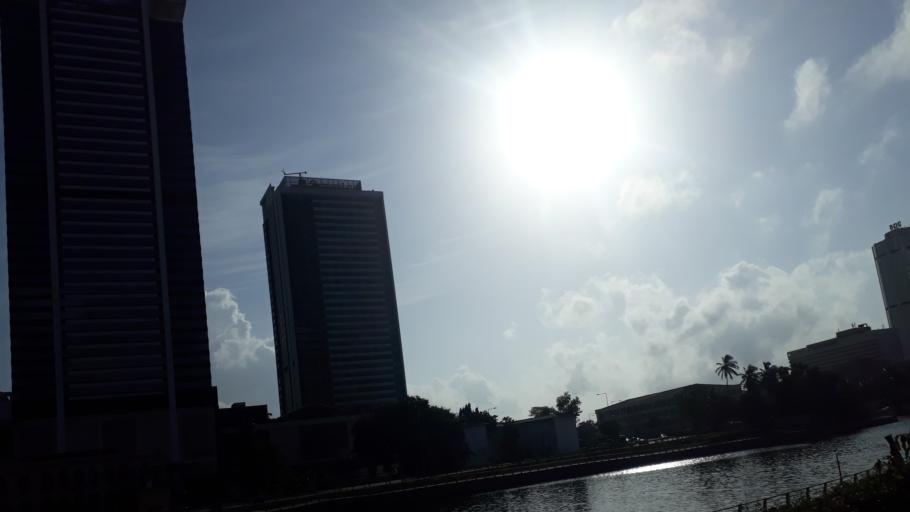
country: LK
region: Western
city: Colombo
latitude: 6.9284
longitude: 79.8474
